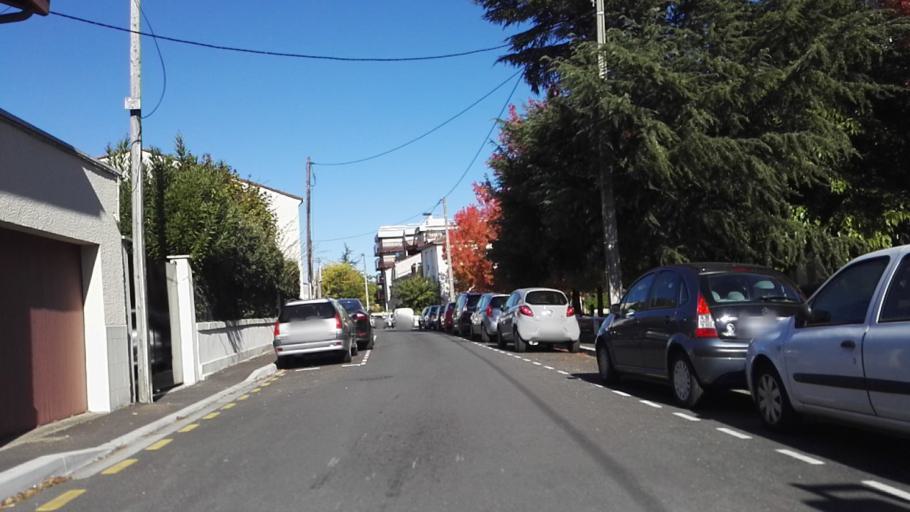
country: FR
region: Aquitaine
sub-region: Departement de la Gironde
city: Merignac
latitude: 44.8442
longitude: -0.6136
